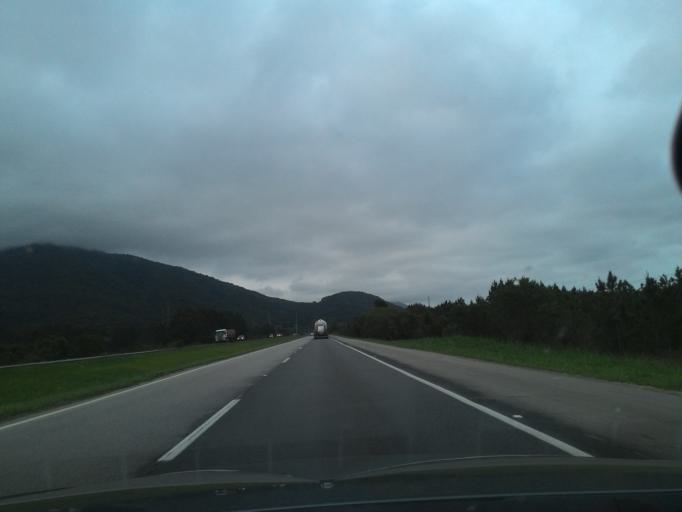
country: BR
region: Santa Catarina
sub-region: Florianopolis
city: Pantano do Sul
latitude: -27.8725
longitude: -48.6465
